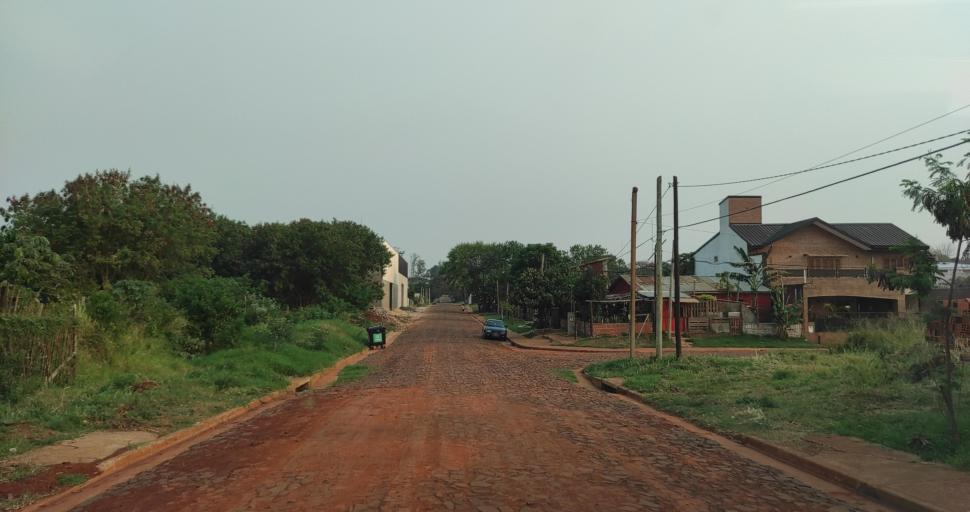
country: AR
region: Misiones
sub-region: Departamento de Capital
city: Posadas
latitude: -27.3965
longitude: -55.9254
